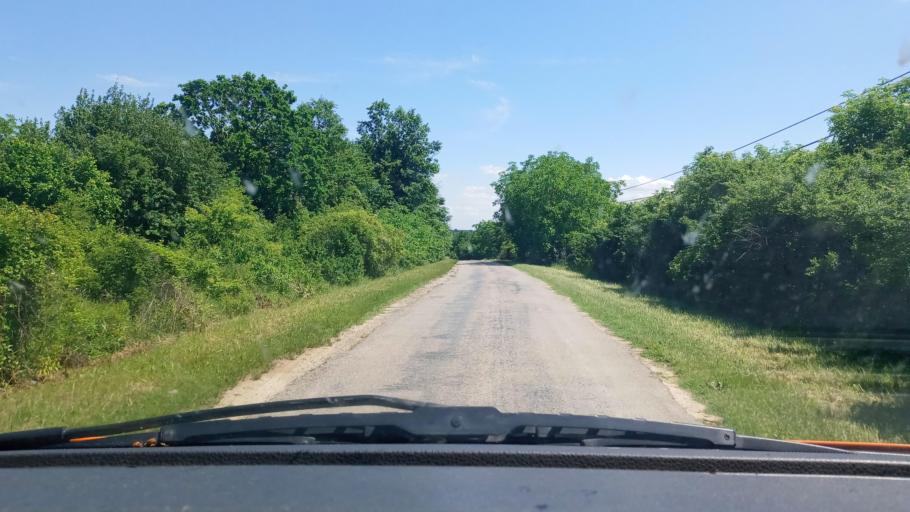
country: HU
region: Somogy
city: Kadarkut
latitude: 46.1769
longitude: 17.7420
